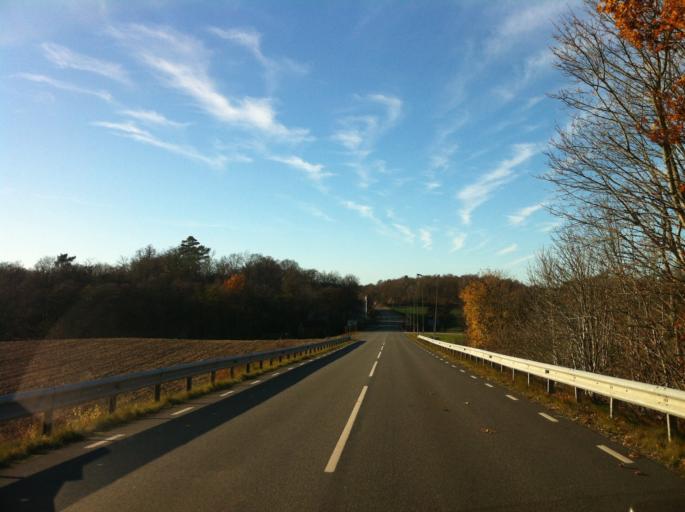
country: SE
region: Blekinge
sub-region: Karlshamns Kommun
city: Karlshamn
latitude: 56.1991
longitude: 14.9485
